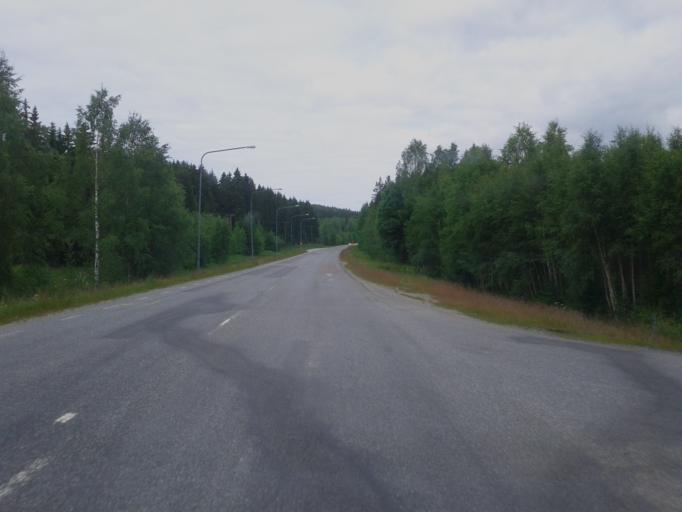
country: SE
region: Vaesternorrland
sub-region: OErnskoeldsviks Kommun
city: Bjasta
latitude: 63.2075
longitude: 18.4832
